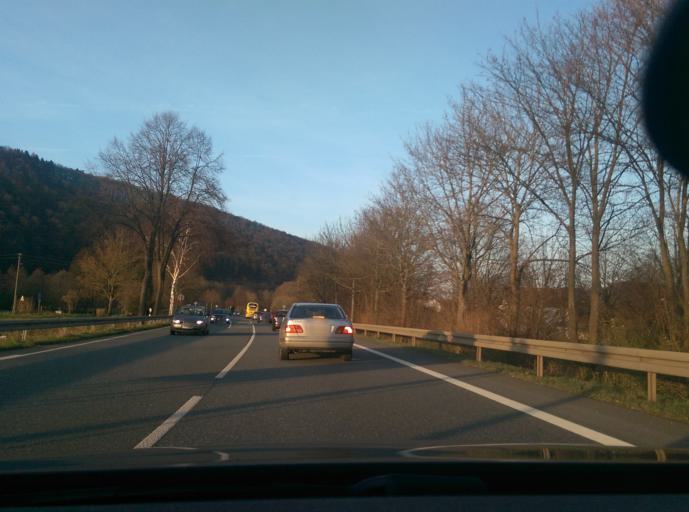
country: DE
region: Hesse
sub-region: Regierungsbezirk Kassel
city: Sontra
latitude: 51.1045
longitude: 9.9669
